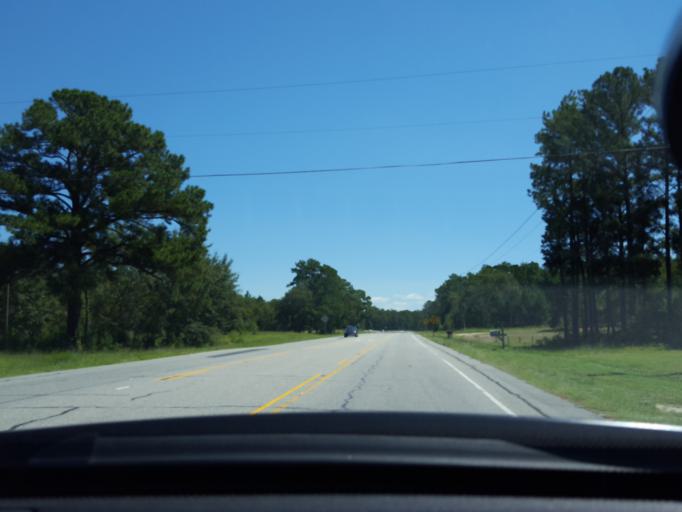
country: US
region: North Carolina
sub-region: Bladen County
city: Elizabethtown
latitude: 34.6478
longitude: -78.5646
